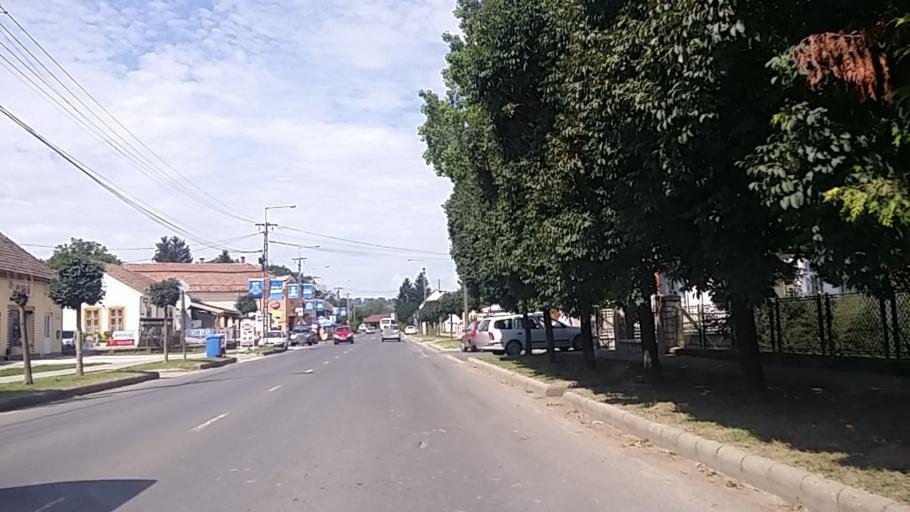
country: HU
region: Baranya
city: Sasd
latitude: 46.2524
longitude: 18.1094
